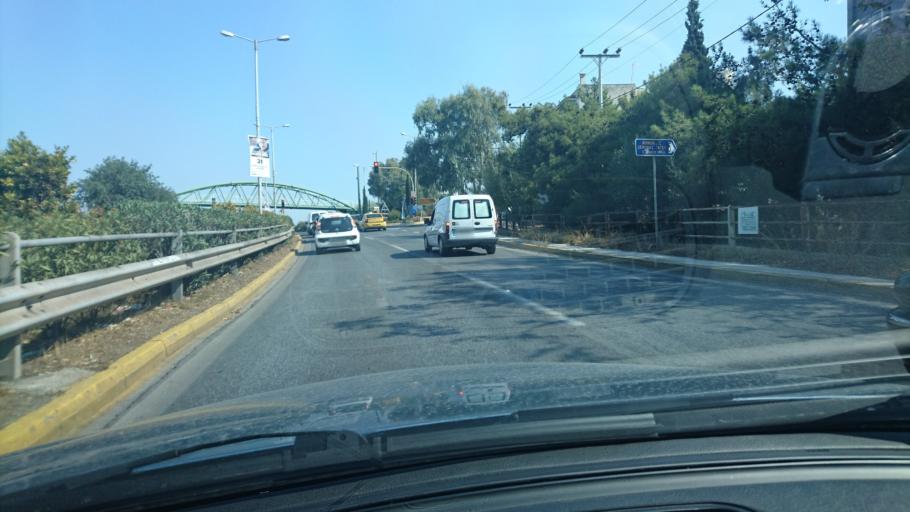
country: GR
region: Attica
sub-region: Nomarchia Athinas
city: Kaisariani
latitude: 37.9484
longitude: 23.7679
